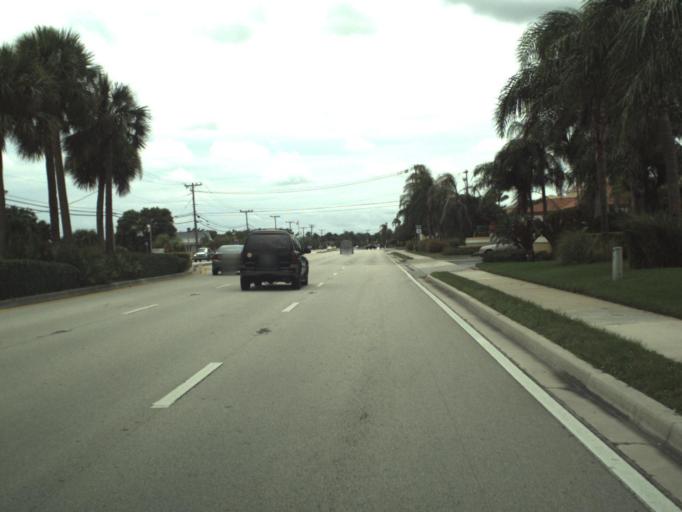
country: US
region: Florida
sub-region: Palm Beach County
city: Jupiter
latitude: 26.9669
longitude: -80.0862
